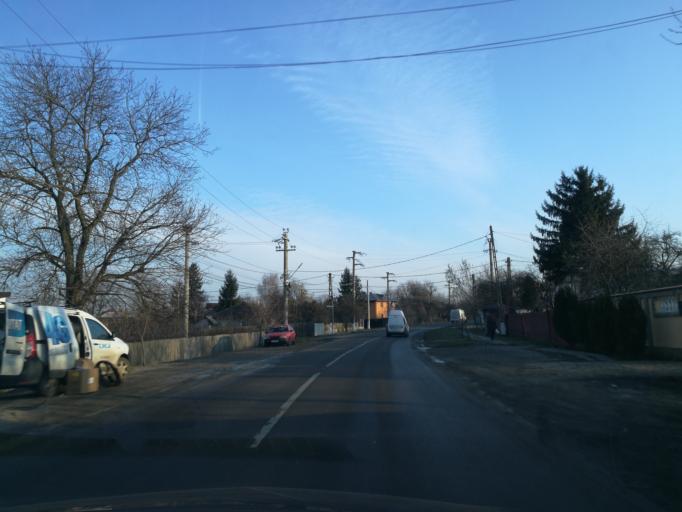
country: RO
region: Ilfov
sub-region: Comuna Moara Vlasiei
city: Moara Vlasiei
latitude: 44.6391
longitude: 26.1978
